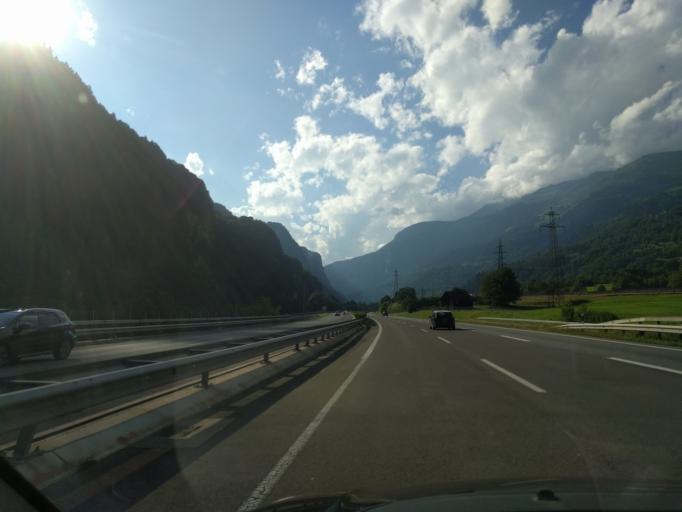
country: CH
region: Ticino
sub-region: Leventina District
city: Faido
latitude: 46.4668
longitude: 8.8184
